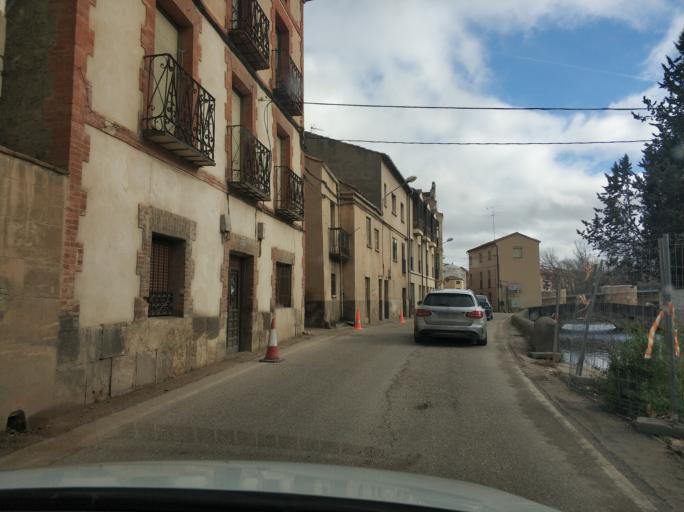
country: ES
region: Castille and Leon
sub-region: Provincia de Soria
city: San Esteban de Gormaz
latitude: 41.5739
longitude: -3.2060
